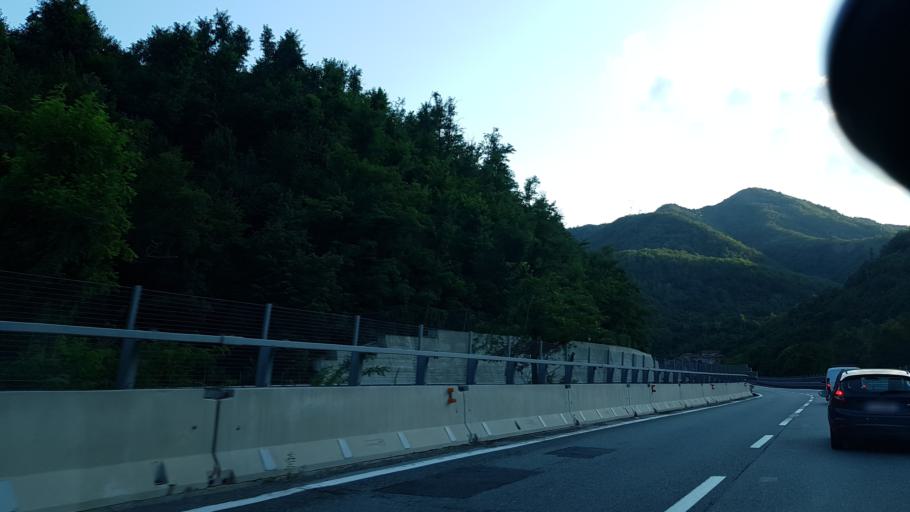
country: IT
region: Liguria
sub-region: Provincia di Genova
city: Isola del Cantone
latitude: 44.6345
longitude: 8.9477
